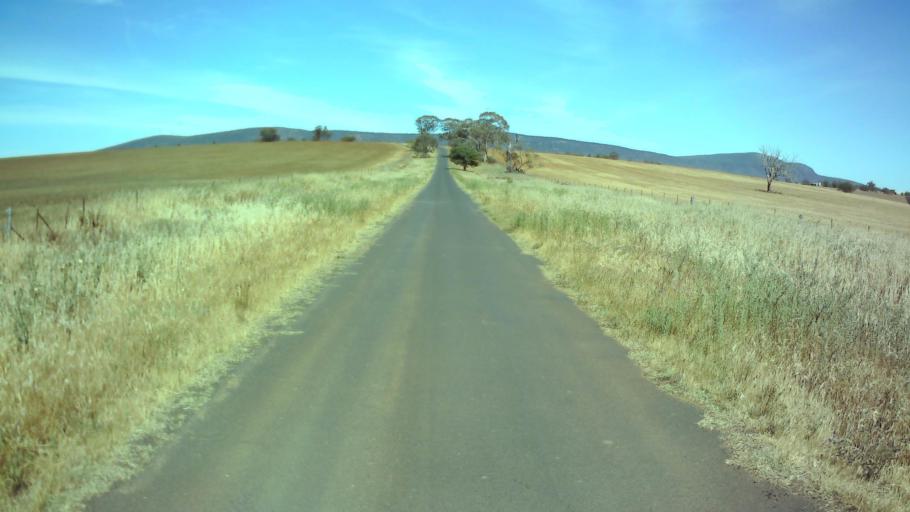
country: AU
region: New South Wales
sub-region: Weddin
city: Grenfell
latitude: -33.9405
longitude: 148.0742
